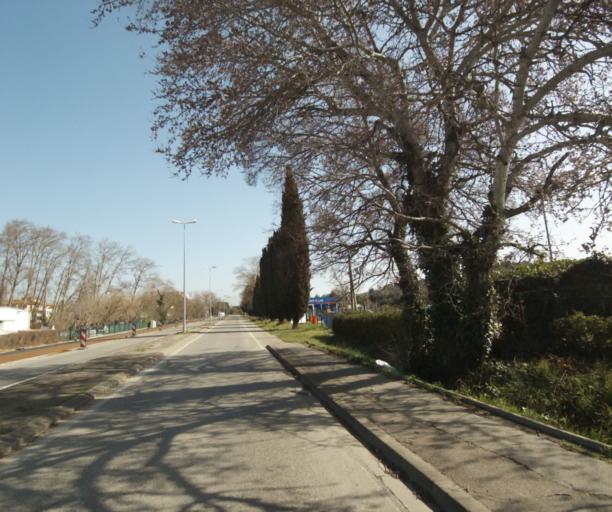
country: FR
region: Provence-Alpes-Cote d'Azur
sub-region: Departement des Bouches-du-Rhone
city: Aix-en-Provence
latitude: 43.5078
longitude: 5.4176
